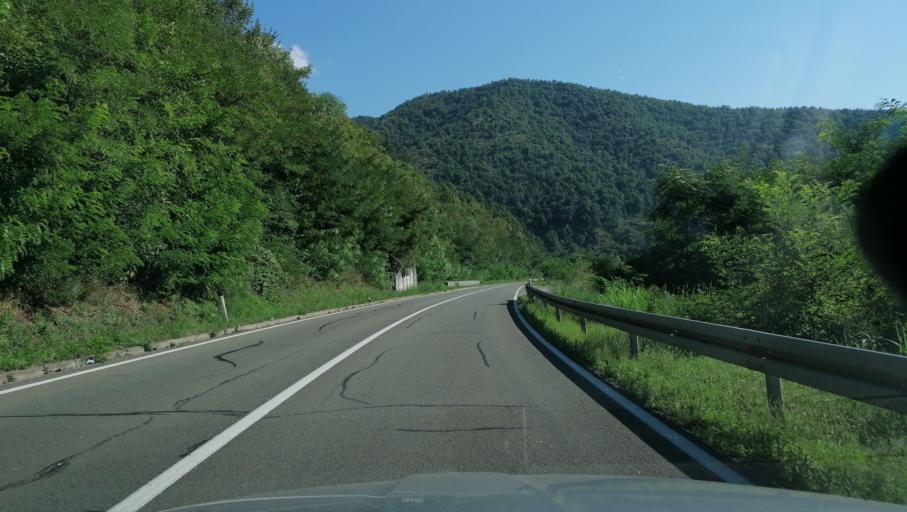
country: RS
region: Central Serbia
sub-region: Raski Okrug
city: Kraljevo
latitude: 43.6632
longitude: 20.5823
